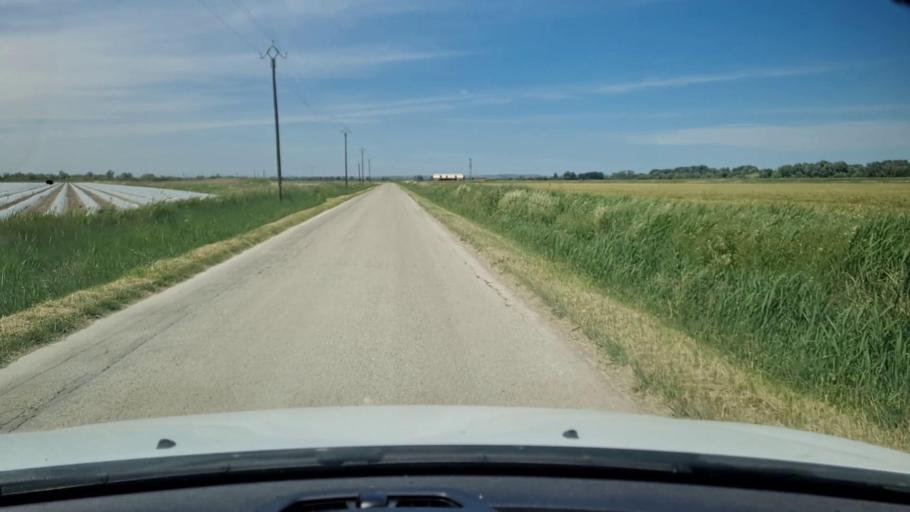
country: FR
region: Languedoc-Roussillon
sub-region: Departement du Gard
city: Saint-Gilles
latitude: 43.6063
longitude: 4.4330
